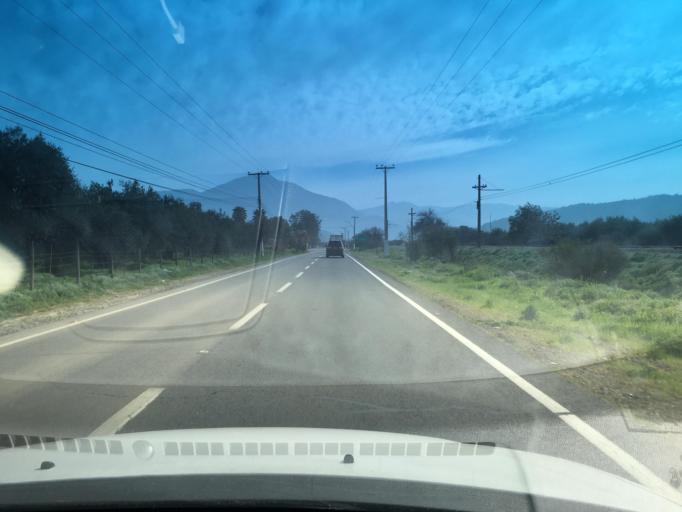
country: CL
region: Santiago Metropolitan
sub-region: Provincia de Chacabuco
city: Lampa
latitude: -33.1173
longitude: -70.9261
